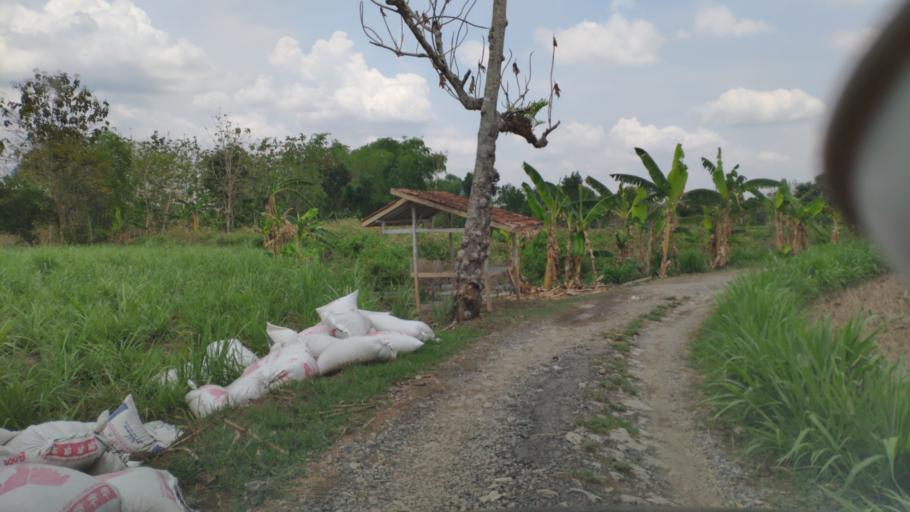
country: ID
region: Central Java
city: Gumiring
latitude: -7.0492
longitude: 111.3948
